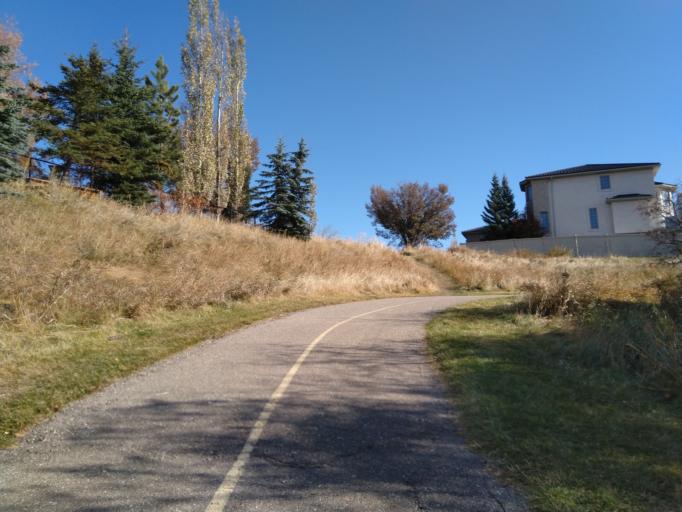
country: CA
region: Alberta
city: Calgary
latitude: 51.1331
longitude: -114.1512
